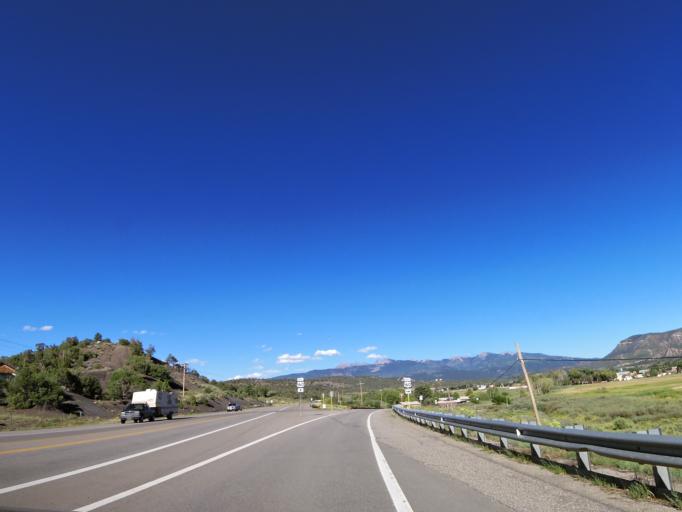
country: US
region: Colorado
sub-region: Montezuma County
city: Mancos
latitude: 37.3442
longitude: -108.3157
